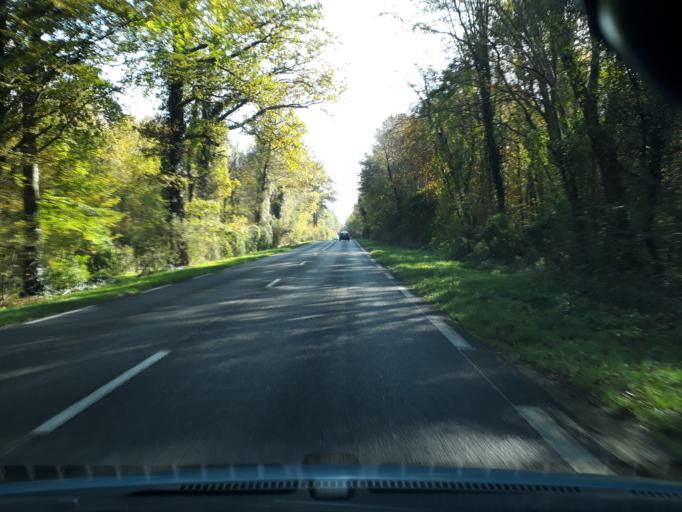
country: FR
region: Ile-de-France
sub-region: Departement de Seine-et-Marne
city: Bois-le-Roi
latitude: 48.4631
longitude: 2.6941
